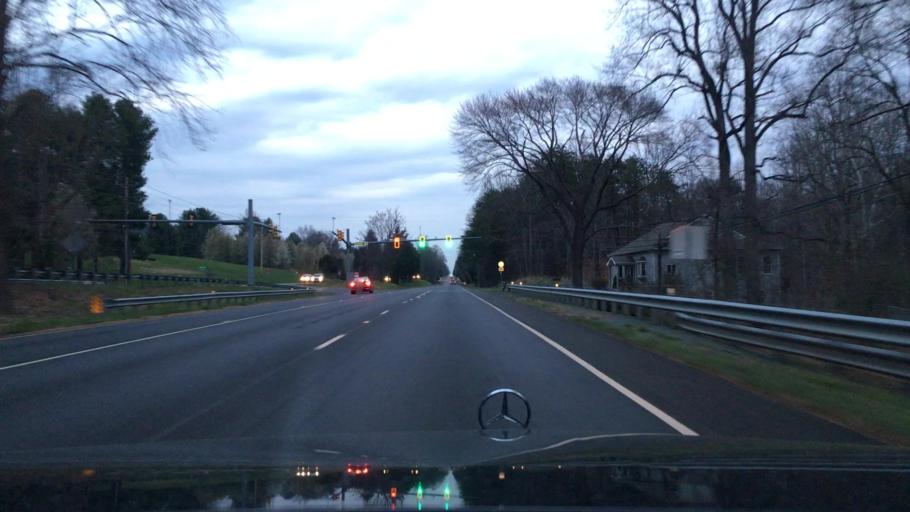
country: US
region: Virginia
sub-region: Albemarle County
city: Hollymead
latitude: 38.1635
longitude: -78.4148
